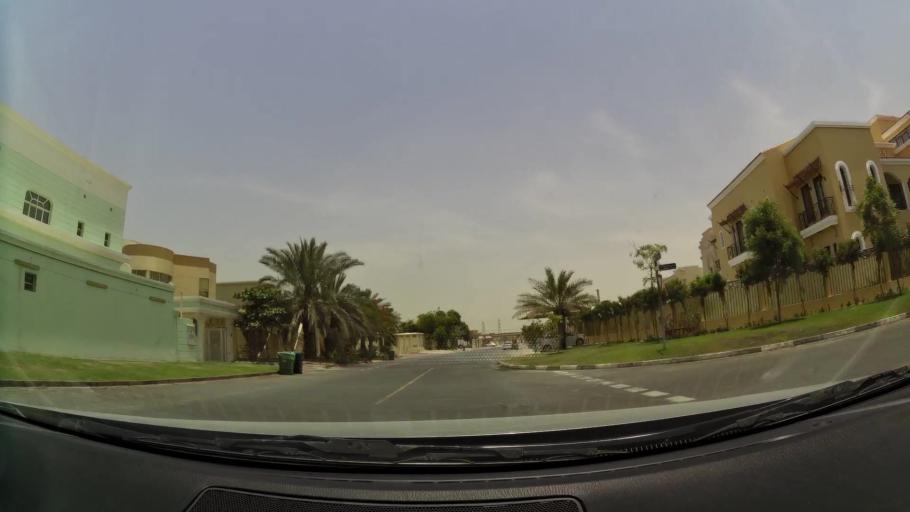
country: AE
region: Ash Shariqah
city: Sharjah
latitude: 25.2115
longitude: 55.3928
